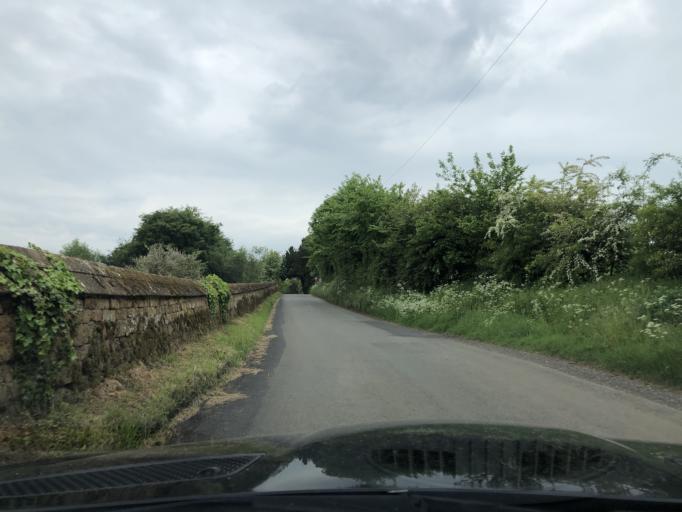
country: GB
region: England
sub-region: Oxfordshire
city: Claydon
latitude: 52.1416
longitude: -1.3679
